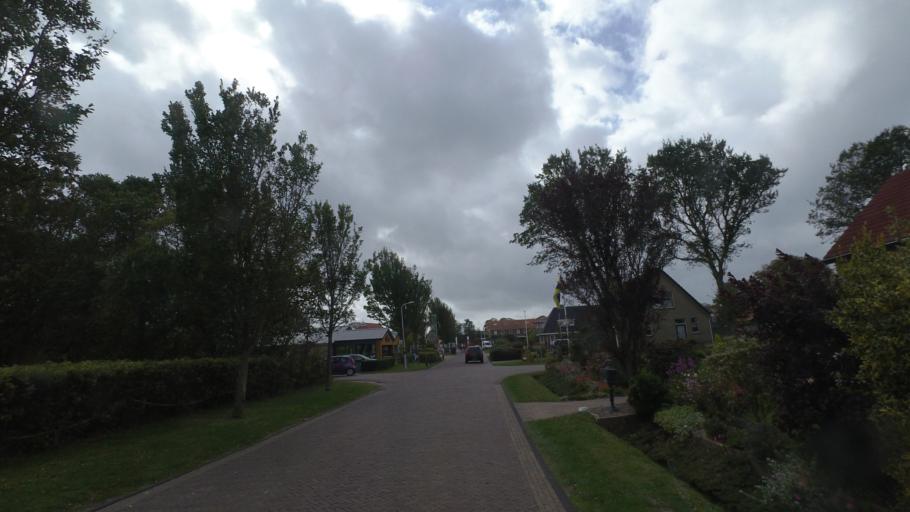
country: NL
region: Friesland
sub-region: Gemeente Ameland
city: Hollum
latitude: 53.4429
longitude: 5.6397
